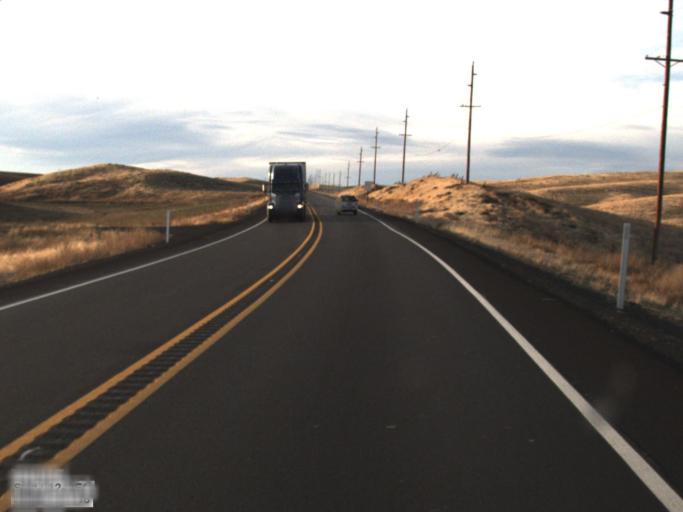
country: US
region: Washington
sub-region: Walla Walla County
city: Garrett
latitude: 46.0529
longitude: -118.7102
